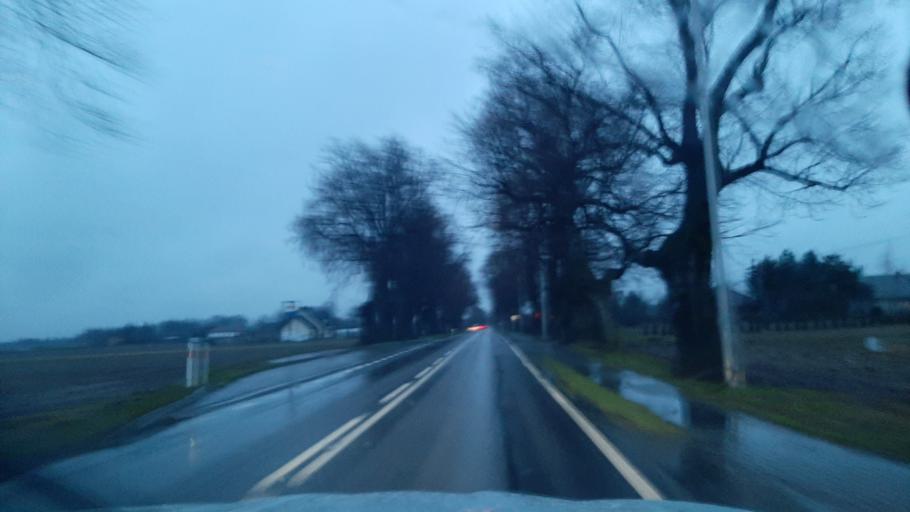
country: PL
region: Lublin Voivodeship
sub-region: Powiat lubelski
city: Jastkow
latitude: 51.3540
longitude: 22.4716
